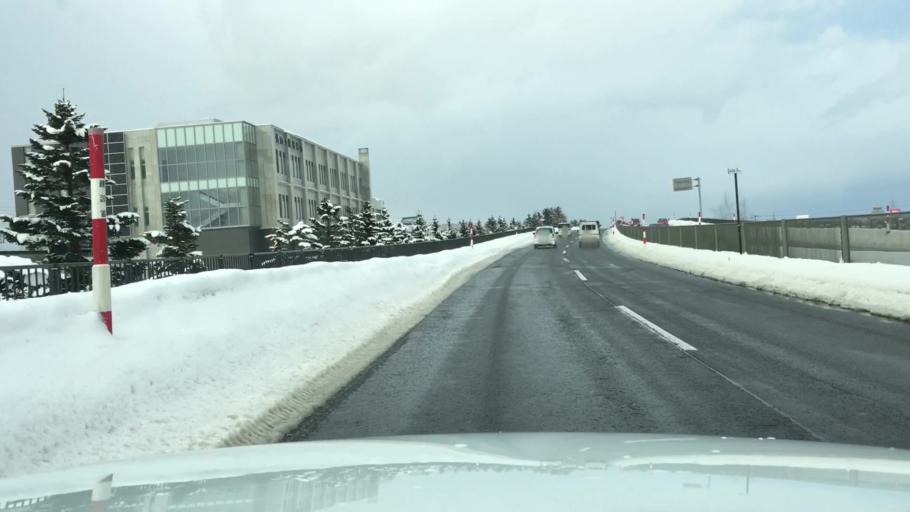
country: JP
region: Aomori
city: Hirosaki
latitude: 40.5868
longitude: 140.5071
